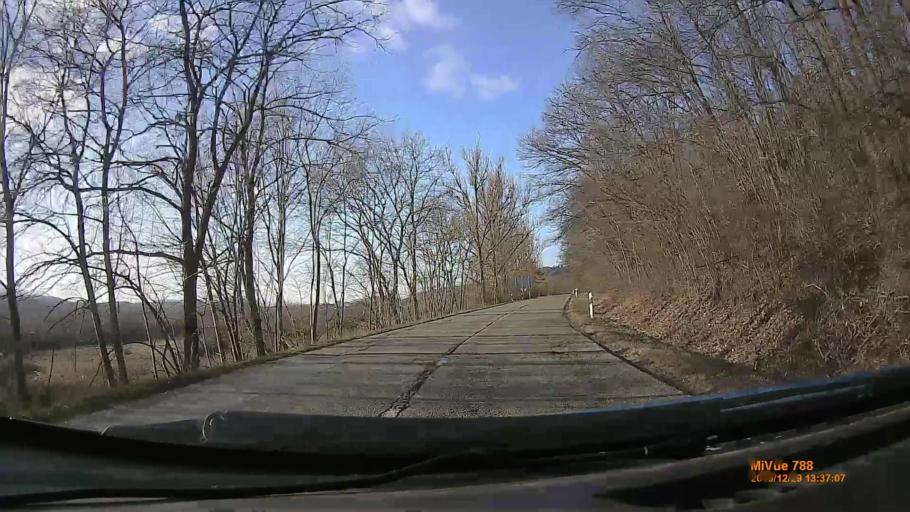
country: HU
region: Heves
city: Sirok
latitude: 47.9213
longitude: 20.1734
